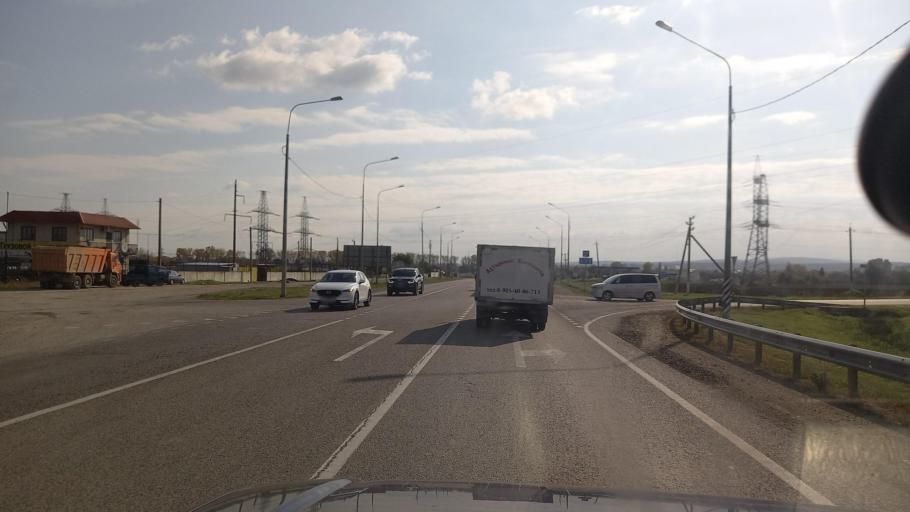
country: RU
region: Krasnodarskiy
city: Novoukrainskiy
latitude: 44.9059
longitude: 38.0279
